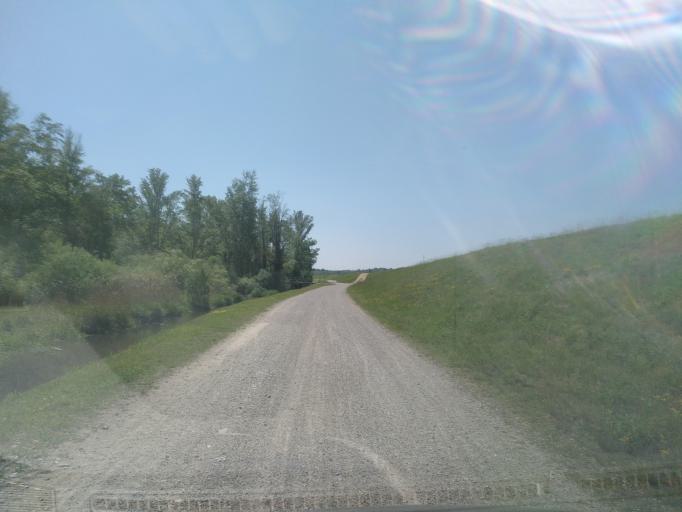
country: FR
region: Alsace
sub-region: Departement du Haut-Rhin
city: Kunheim
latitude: 48.0853
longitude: 7.5721
